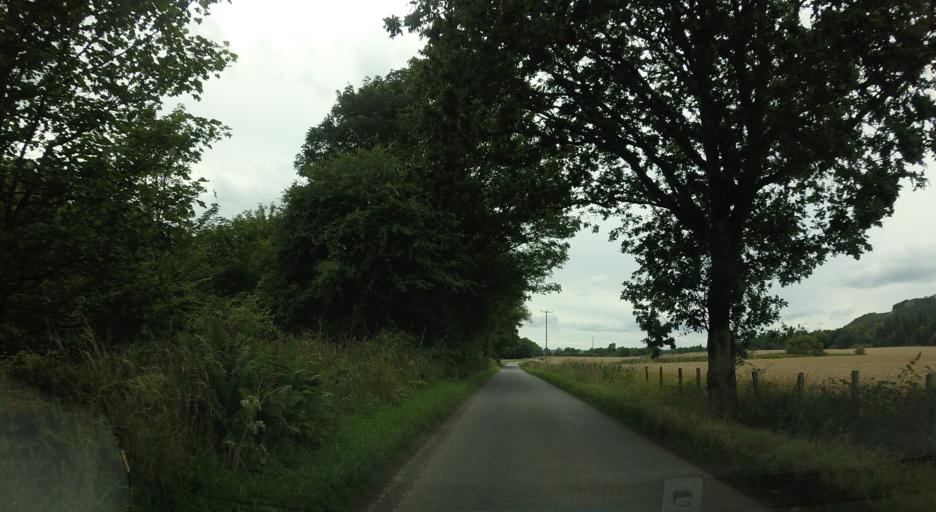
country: GB
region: Scotland
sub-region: Perth and Kinross
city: Bridge of Earn
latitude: 56.3540
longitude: -3.3876
